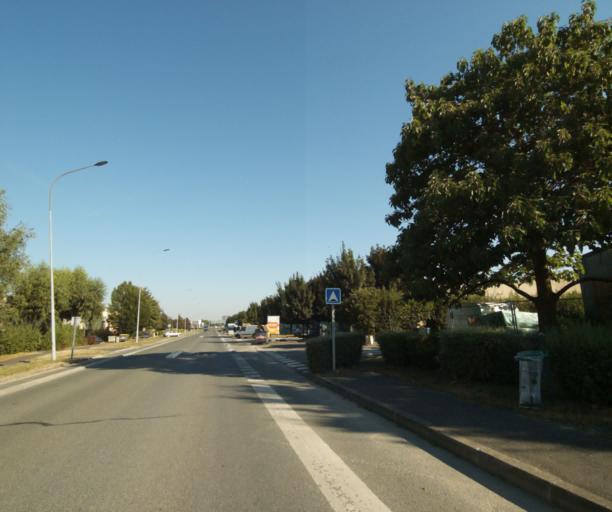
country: FR
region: Ile-de-France
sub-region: Departement de Seine-et-Marne
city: Lieusaint
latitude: 48.6218
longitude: 2.5676
